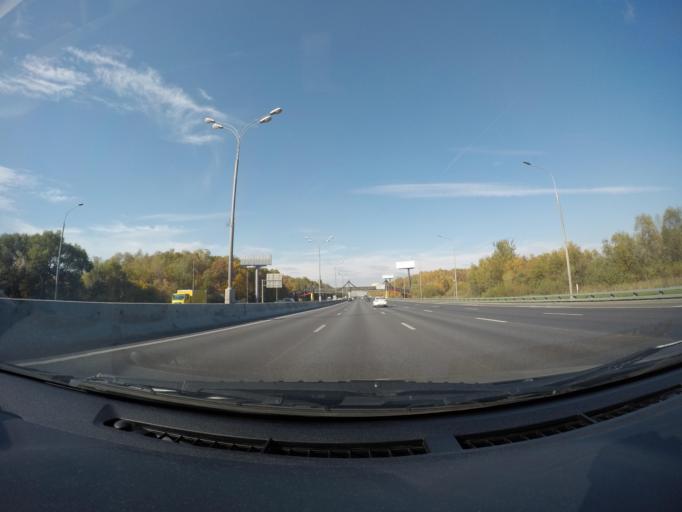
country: RU
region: Moscow
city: Gol'yanovo
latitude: 55.8314
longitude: 37.8253
